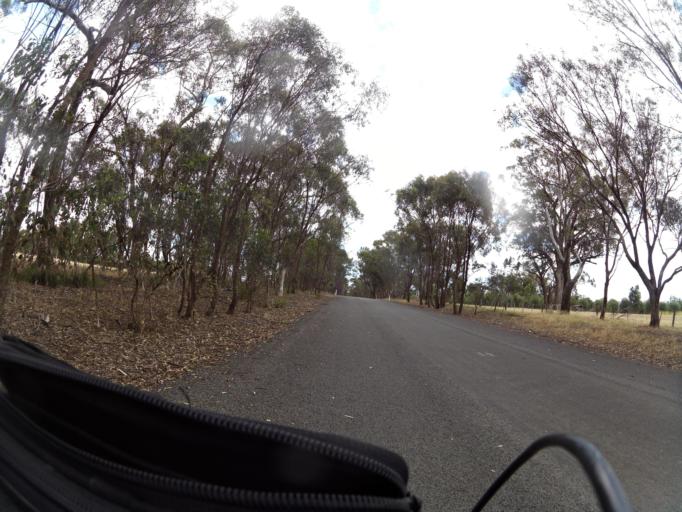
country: AU
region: Victoria
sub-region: Greater Shepparton
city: Shepparton
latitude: -36.7312
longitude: 145.1536
